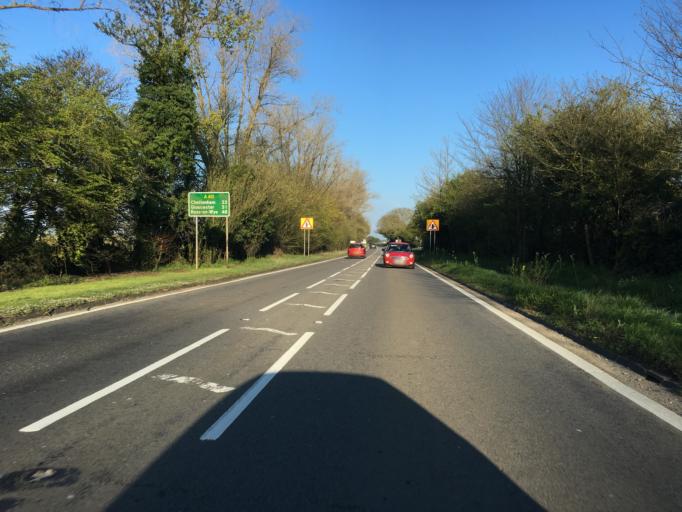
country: GB
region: England
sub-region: Oxfordshire
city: Burford
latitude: 51.8040
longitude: -1.6417
